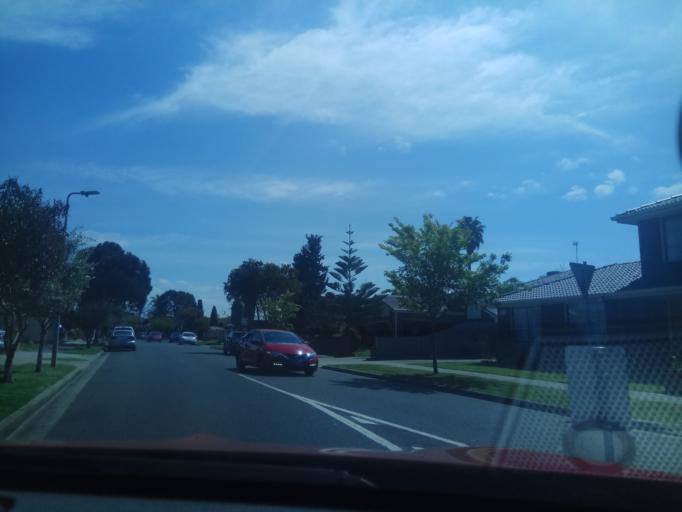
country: AU
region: Victoria
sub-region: Kingston
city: Aspendale Gardens
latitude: -38.0234
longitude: 145.1220
